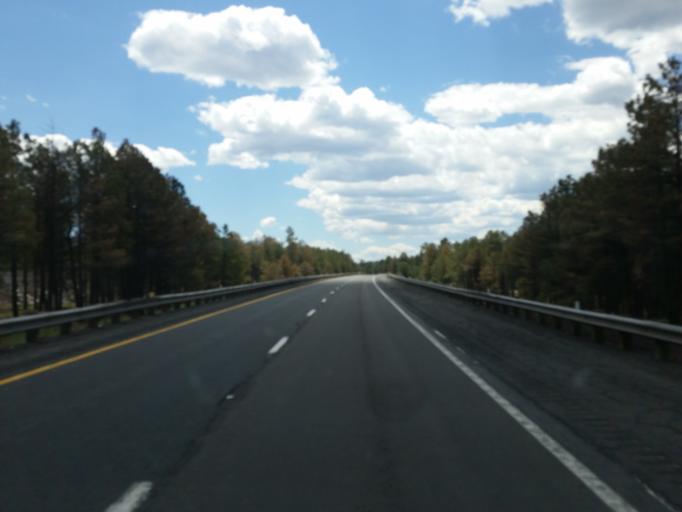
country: US
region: Arizona
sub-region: Coconino County
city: Flagstaff
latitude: 35.2204
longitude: -111.7917
